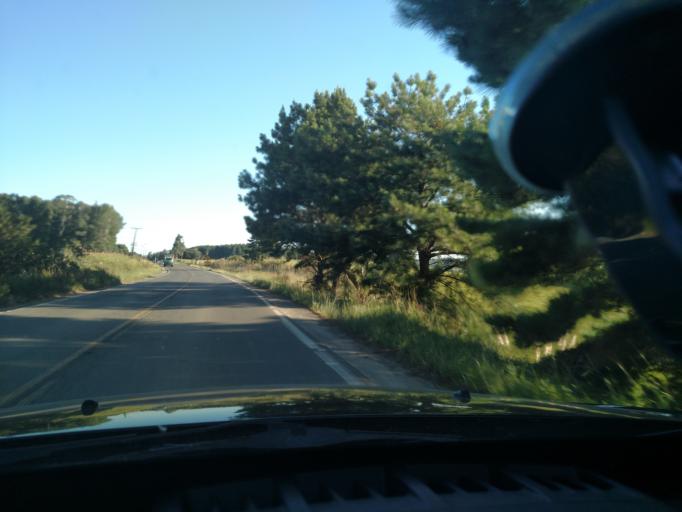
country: BR
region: Santa Catarina
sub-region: Lages
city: Lages
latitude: -27.7123
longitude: -50.2053
